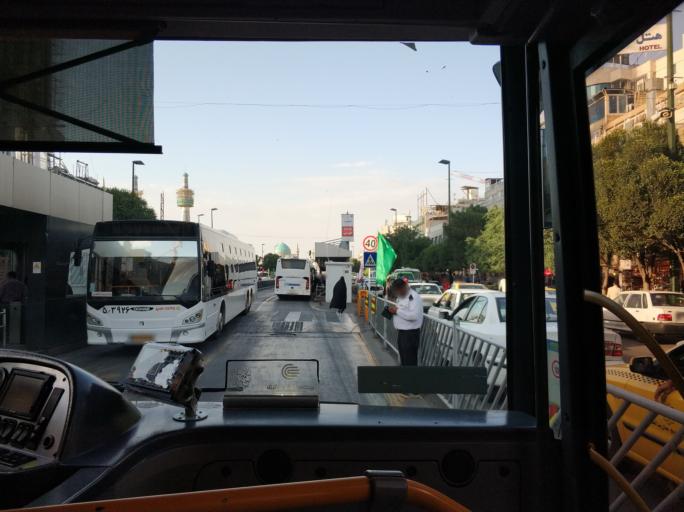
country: IR
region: Razavi Khorasan
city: Mashhad
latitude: 36.2826
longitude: 59.6112
